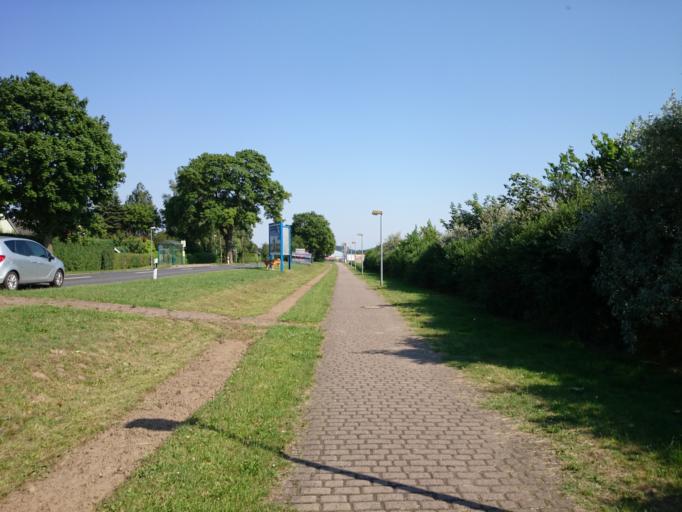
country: DE
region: Mecklenburg-Vorpommern
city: Tessin
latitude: 54.0323
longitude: 12.4470
